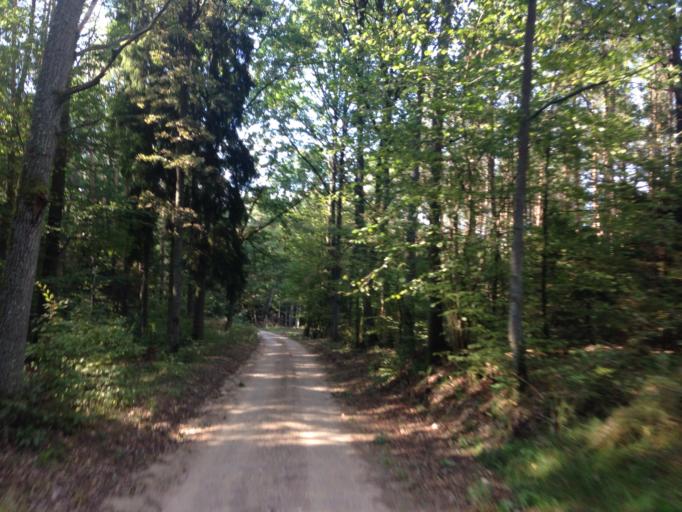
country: PL
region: Kujawsko-Pomorskie
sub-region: Powiat brodnicki
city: Gorzno
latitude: 53.2280
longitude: 19.7089
